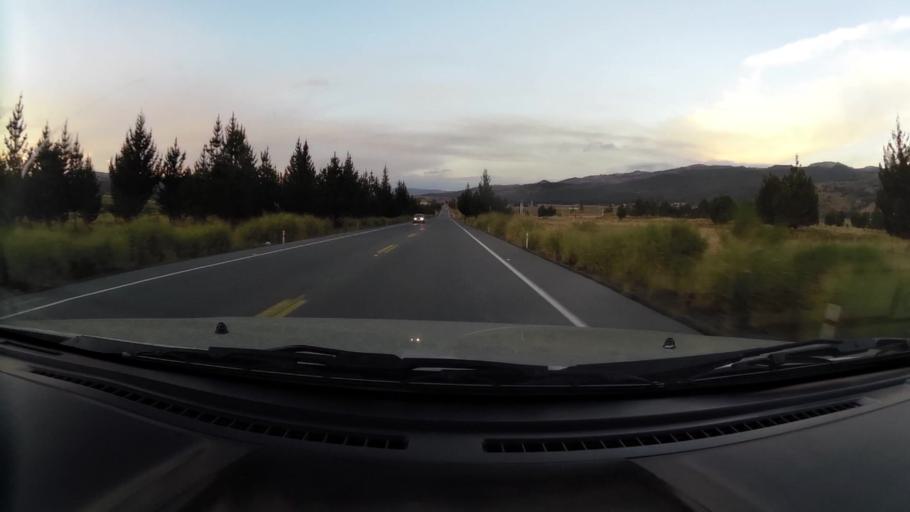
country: EC
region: Chimborazo
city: Alausi
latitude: -2.0261
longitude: -78.7339
